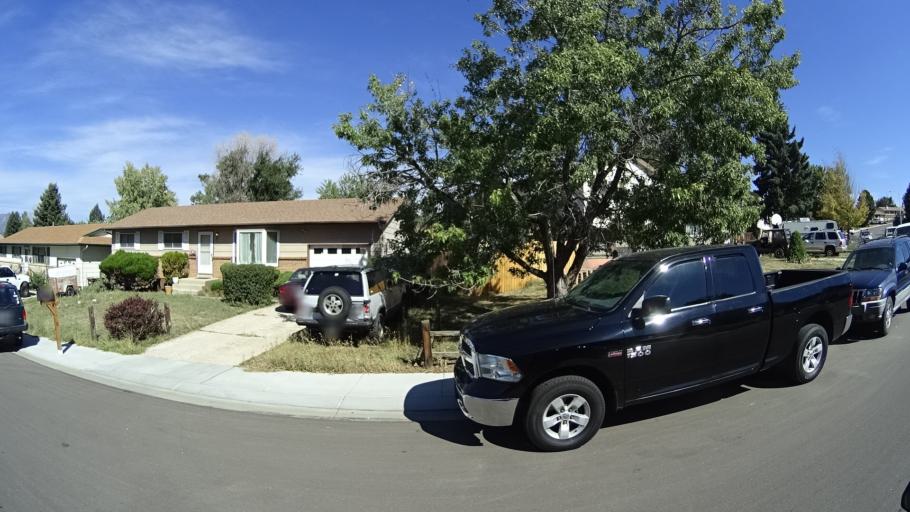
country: US
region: Colorado
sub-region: El Paso County
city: Colorado Springs
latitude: 38.9125
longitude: -104.7831
